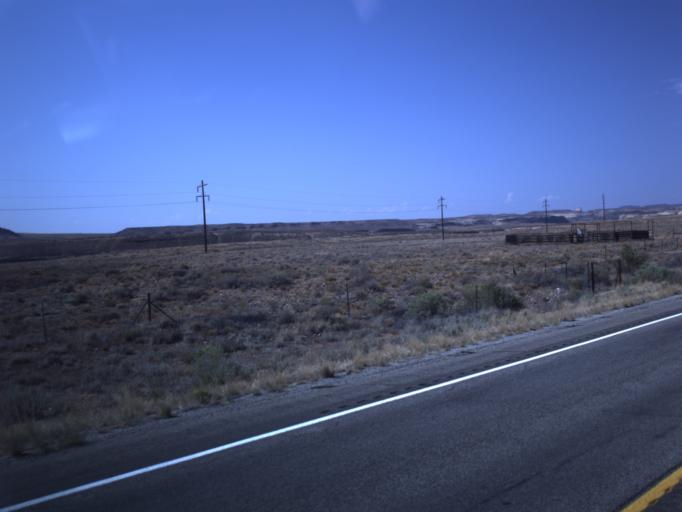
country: US
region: Utah
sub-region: San Juan County
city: Blanding
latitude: 37.2690
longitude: -109.6018
